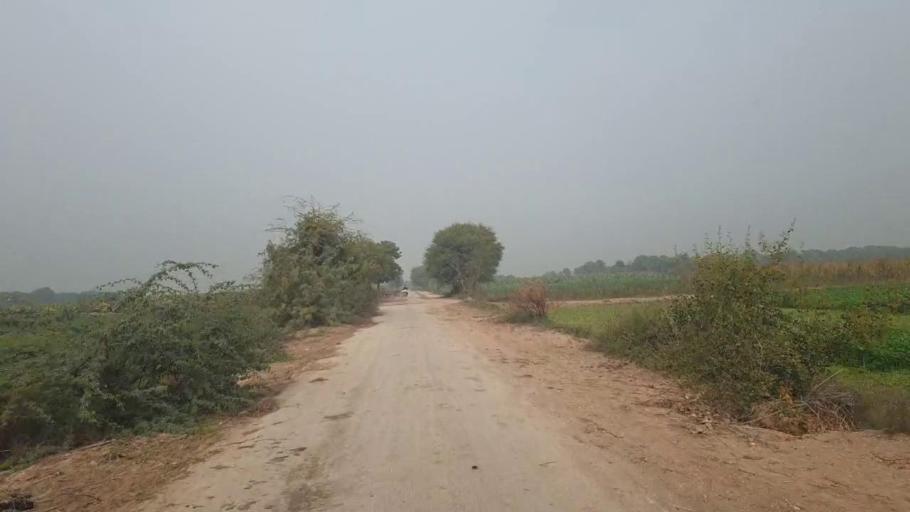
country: PK
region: Sindh
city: Tando Adam
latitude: 25.7615
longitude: 68.7026
